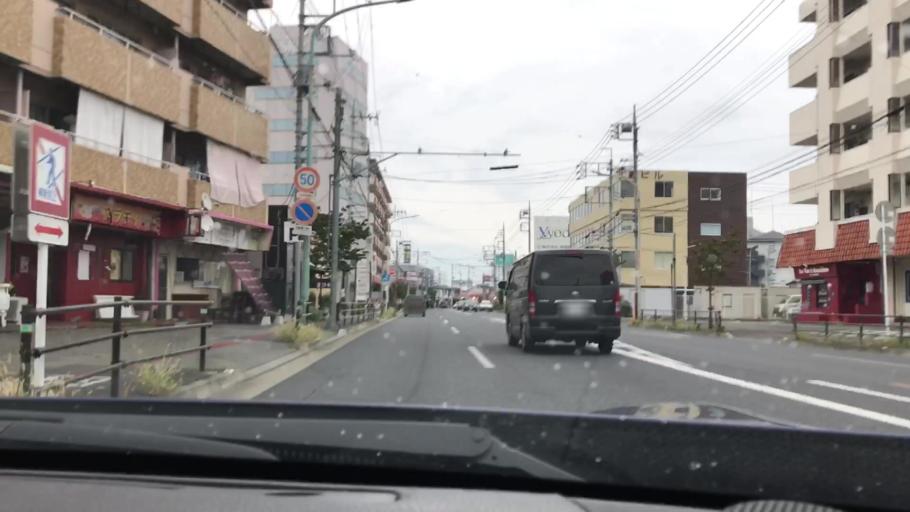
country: JP
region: Gunma
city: Maebashi-shi
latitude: 36.3755
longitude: 139.0653
